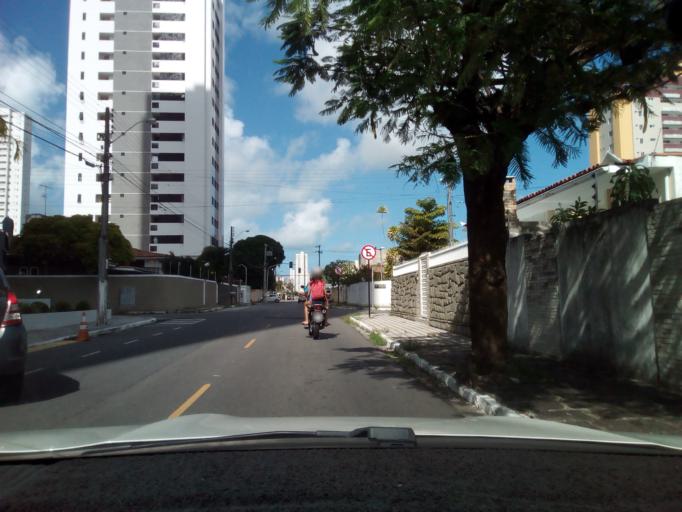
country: BR
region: Paraiba
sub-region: Joao Pessoa
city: Joao Pessoa
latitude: -7.1156
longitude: -34.8543
